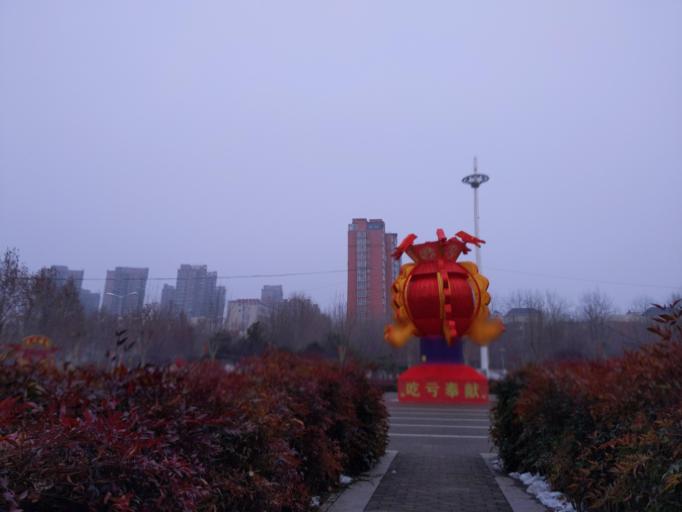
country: CN
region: Henan Sheng
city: Puyang
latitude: 35.7804
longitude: 115.0268
